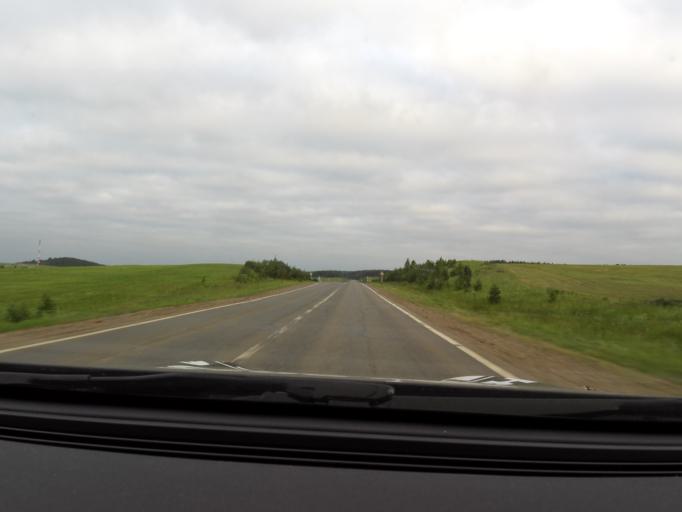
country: RU
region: Perm
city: Siva
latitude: 58.4182
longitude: 54.4616
